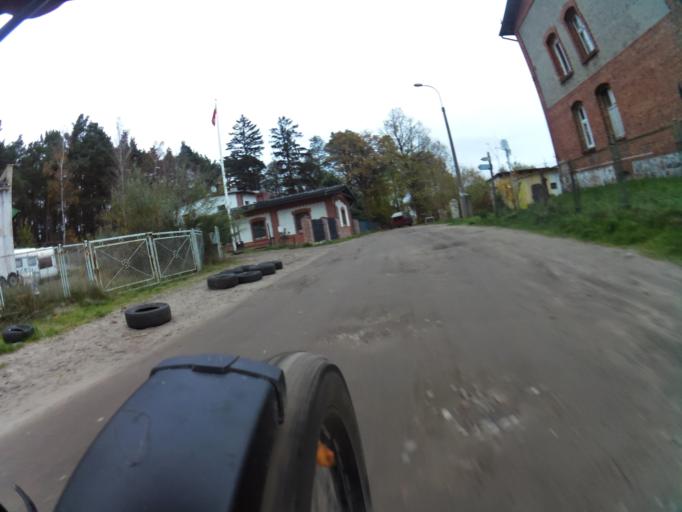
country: PL
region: Pomeranian Voivodeship
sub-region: Powiat wejherowski
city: Choczewo
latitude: 54.7813
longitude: 17.7385
